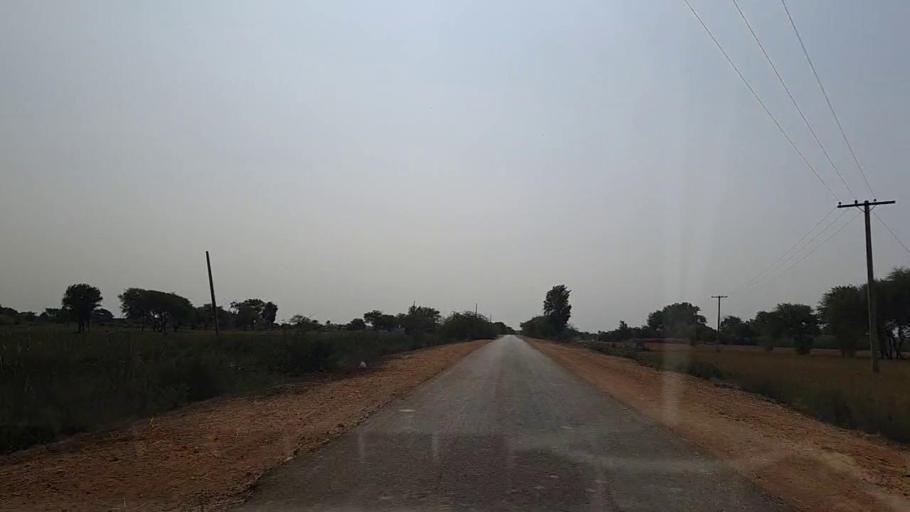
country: PK
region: Sindh
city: Chuhar Jamali
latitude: 24.3177
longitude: 67.9404
